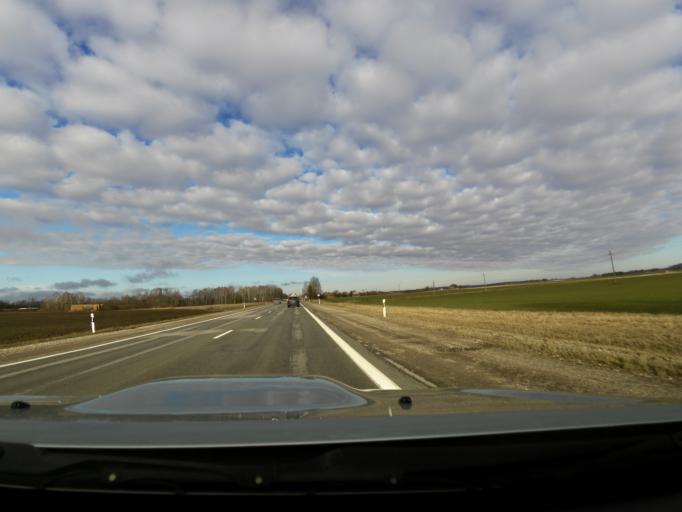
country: LT
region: Panevezys
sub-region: Panevezys City
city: Panevezys
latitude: 55.7516
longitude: 24.1371
